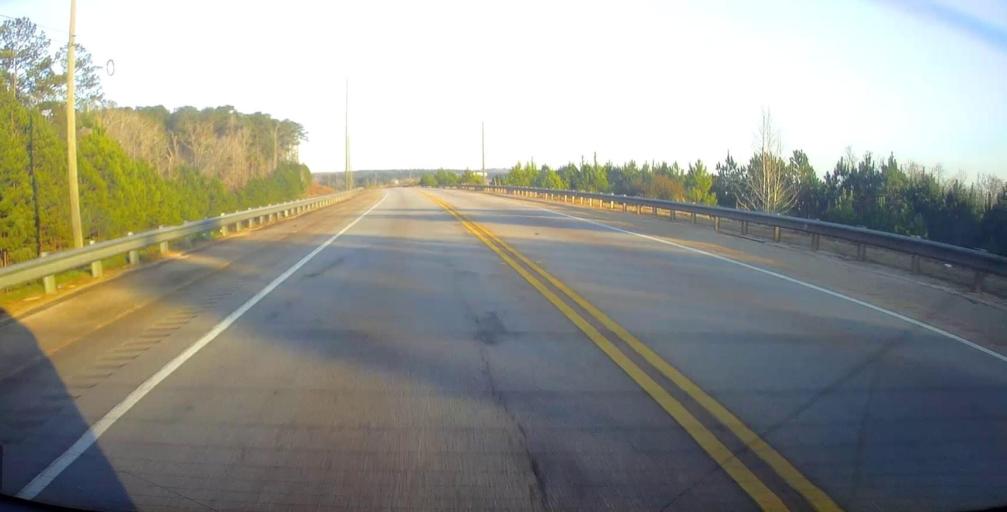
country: US
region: Georgia
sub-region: Troup County
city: La Grange
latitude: 32.9909
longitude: -85.0700
